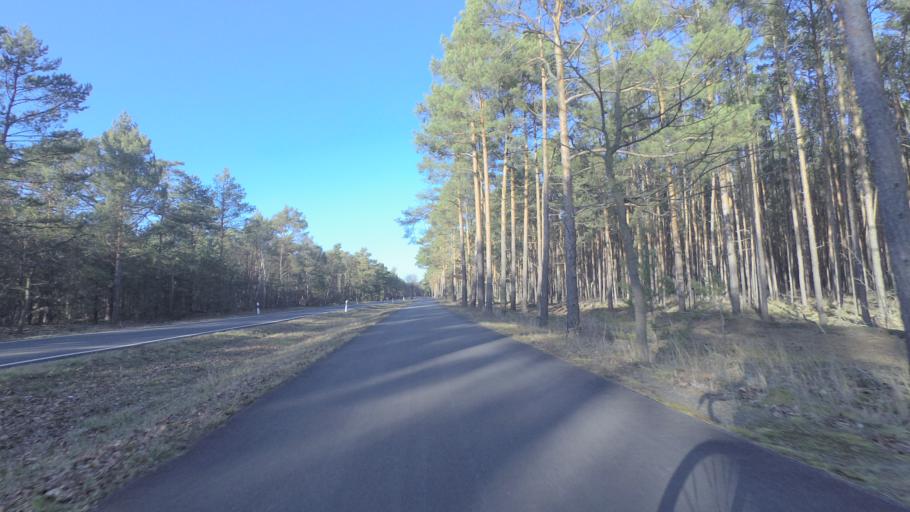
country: DE
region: Brandenburg
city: Sperenberg
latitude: 52.0289
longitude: 13.3185
